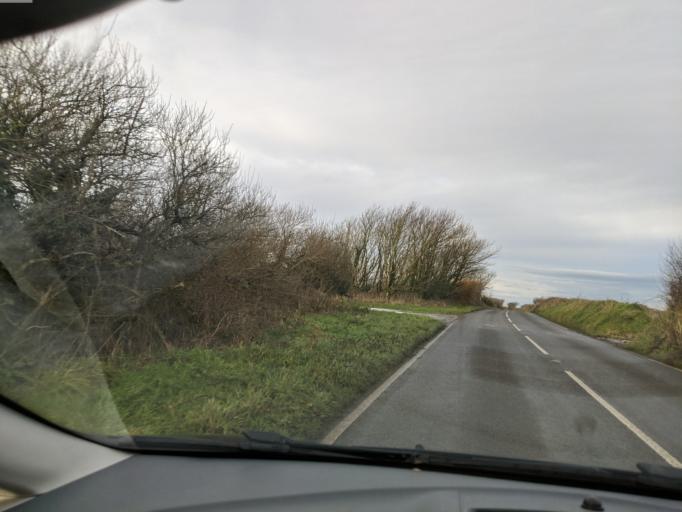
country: GB
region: England
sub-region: Cornwall
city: Jacobstow
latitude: 50.6866
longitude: -4.6151
